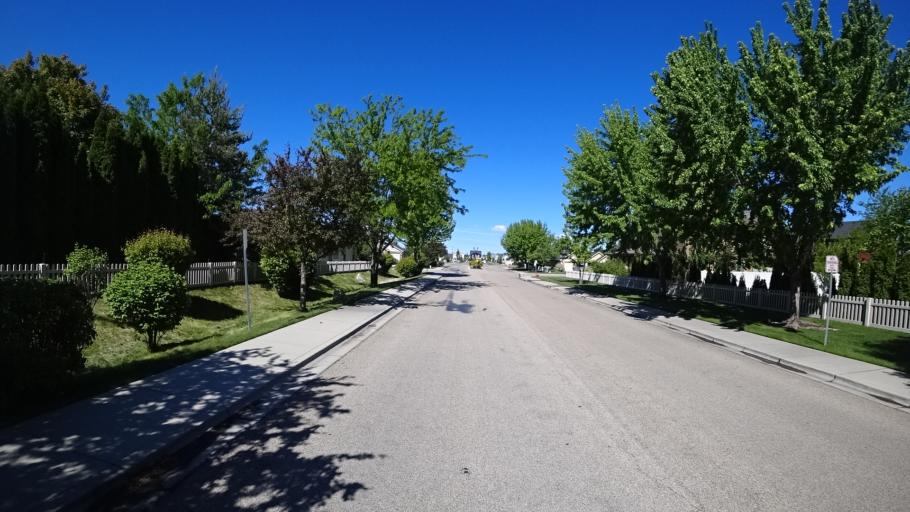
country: US
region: Idaho
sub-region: Ada County
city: Meridian
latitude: 43.6421
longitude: -116.3920
